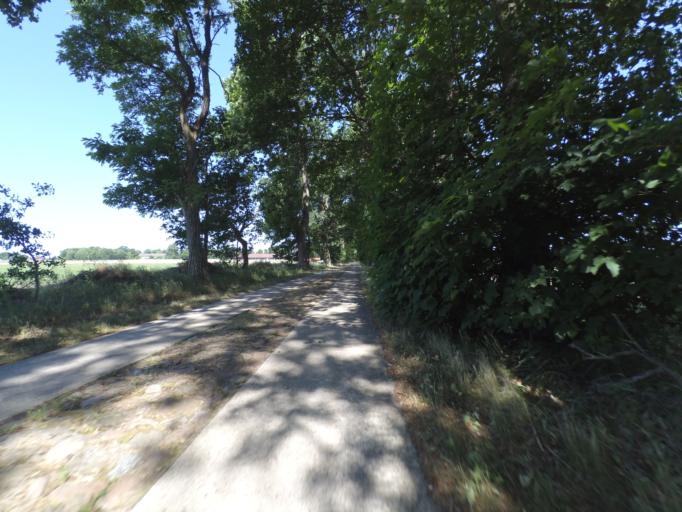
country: DE
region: Brandenburg
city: Heiligengrabe
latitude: 53.2205
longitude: 12.3274
